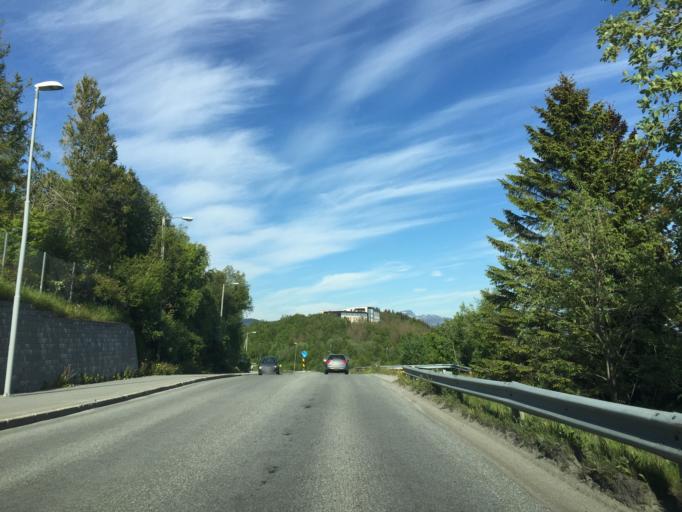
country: NO
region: Nordland
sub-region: Bodo
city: Lopsmarka
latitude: 67.2832
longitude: 14.5499
